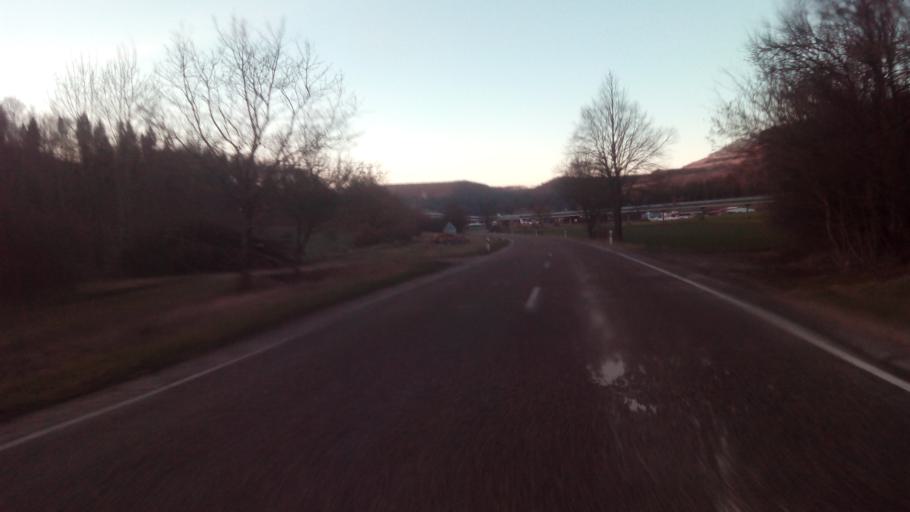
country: DE
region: Baden-Wuerttemberg
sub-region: Tuebingen Region
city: Schelklingen
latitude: 48.3603
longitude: 9.7453
